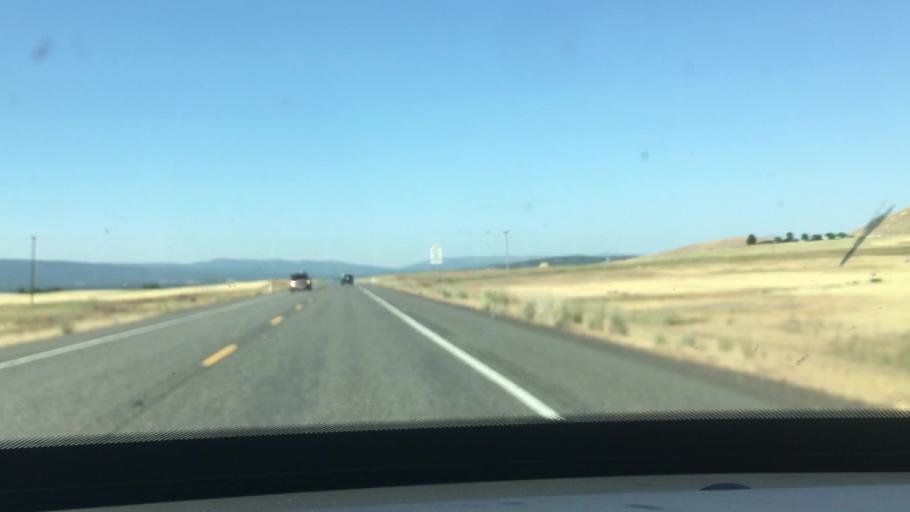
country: US
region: Washington
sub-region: Klickitat County
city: Goldendale
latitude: 45.7939
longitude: -120.8182
